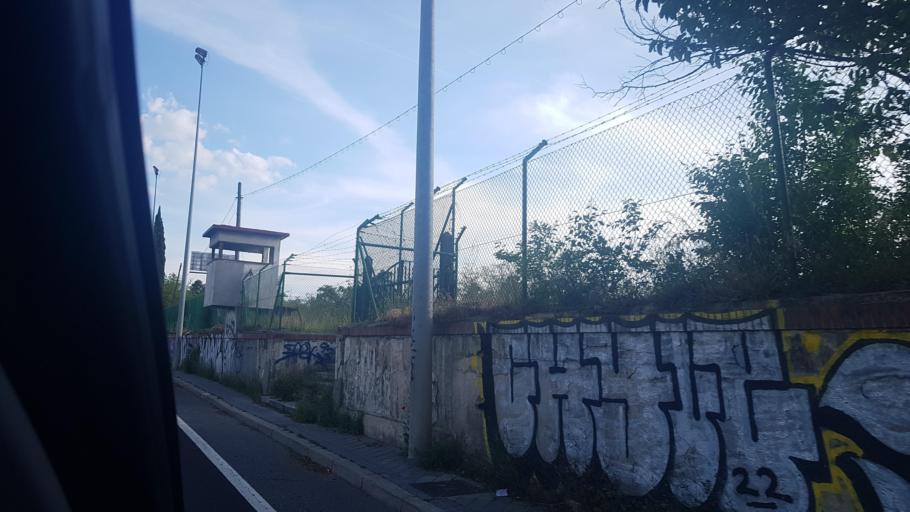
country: ES
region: Madrid
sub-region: Provincia de Madrid
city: Villaverde
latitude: 40.3387
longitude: -3.6928
